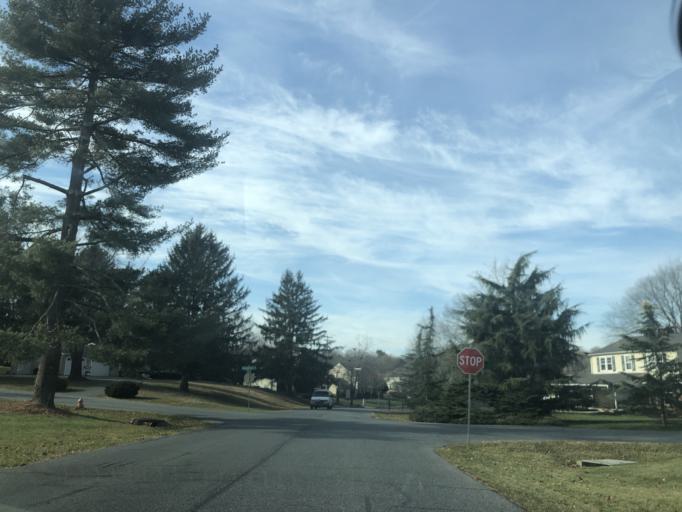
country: US
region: Maryland
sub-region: Howard County
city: Columbia
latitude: 39.2873
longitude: -76.8414
